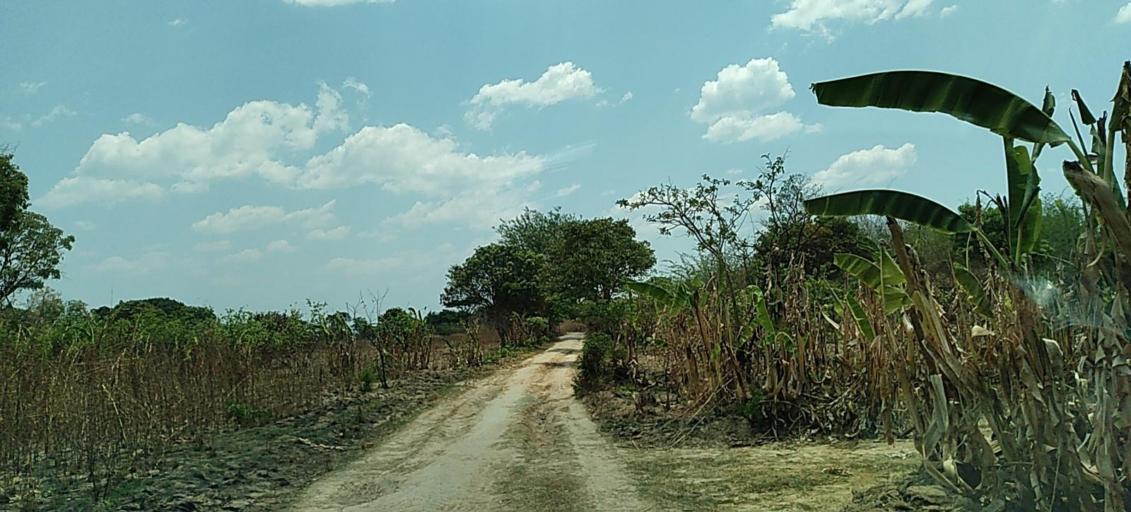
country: ZM
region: Copperbelt
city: Chililabombwe
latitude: -12.4620
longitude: 27.6692
